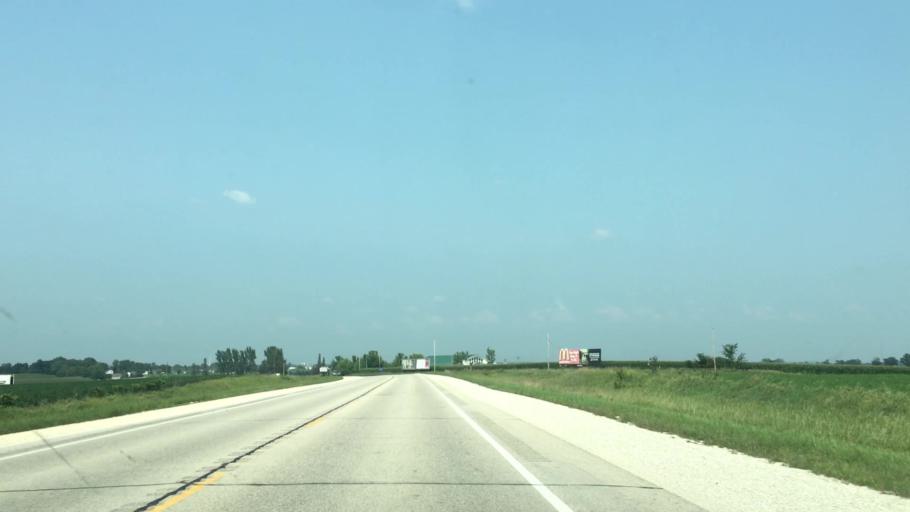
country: US
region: Iowa
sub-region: Winneshiek County
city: Decorah
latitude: 43.2520
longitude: -91.8401
